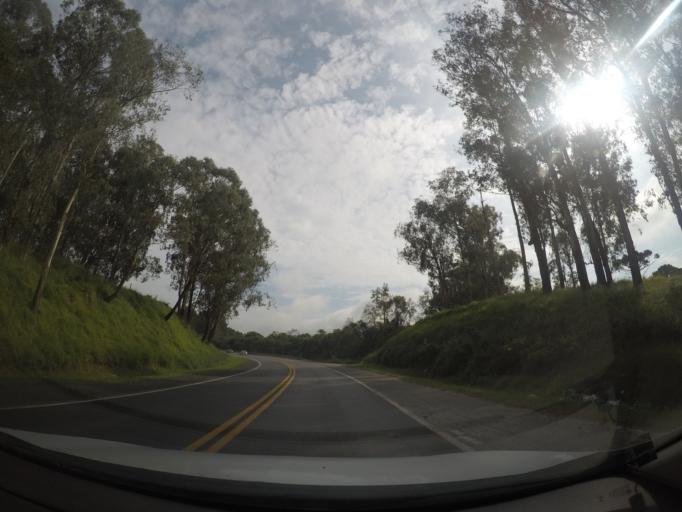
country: BR
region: Parana
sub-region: Colombo
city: Colombo
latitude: -25.3391
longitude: -49.2412
